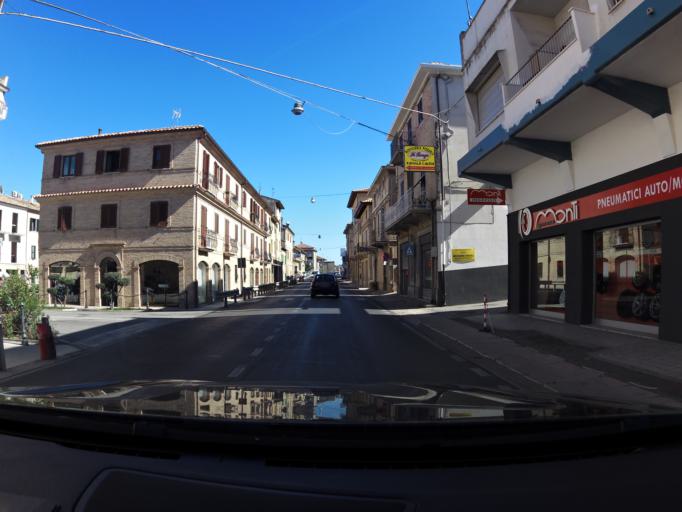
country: IT
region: The Marches
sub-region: Province of Fermo
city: Porto San Giorgio
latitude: 43.1769
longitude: 13.7949
